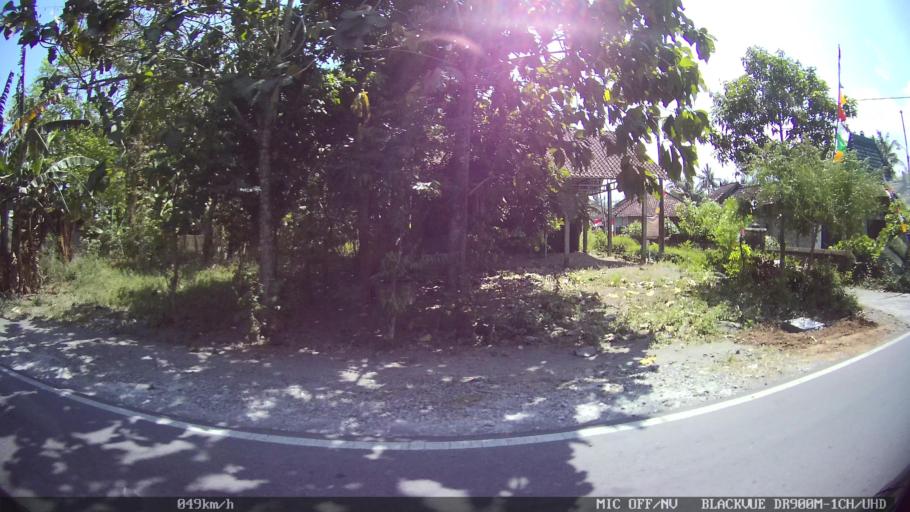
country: ID
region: Daerah Istimewa Yogyakarta
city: Srandakan
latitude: -7.9377
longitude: 110.2570
